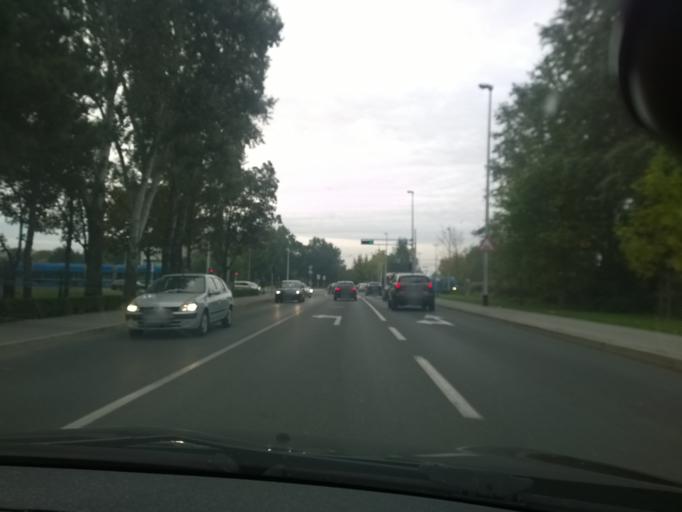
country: HR
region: Grad Zagreb
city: Jankomir
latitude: 45.7946
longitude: 15.8921
